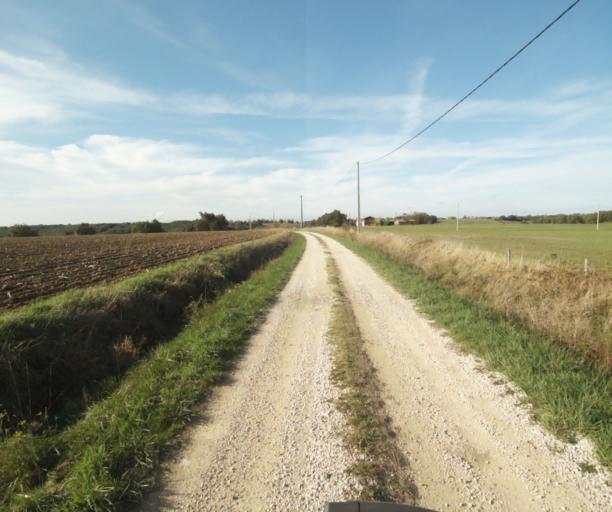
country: FR
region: Midi-Pyrenees
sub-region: Departement du Tarn-et-Garonne
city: Saint-Porquier
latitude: 43.9240
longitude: 1.1252
